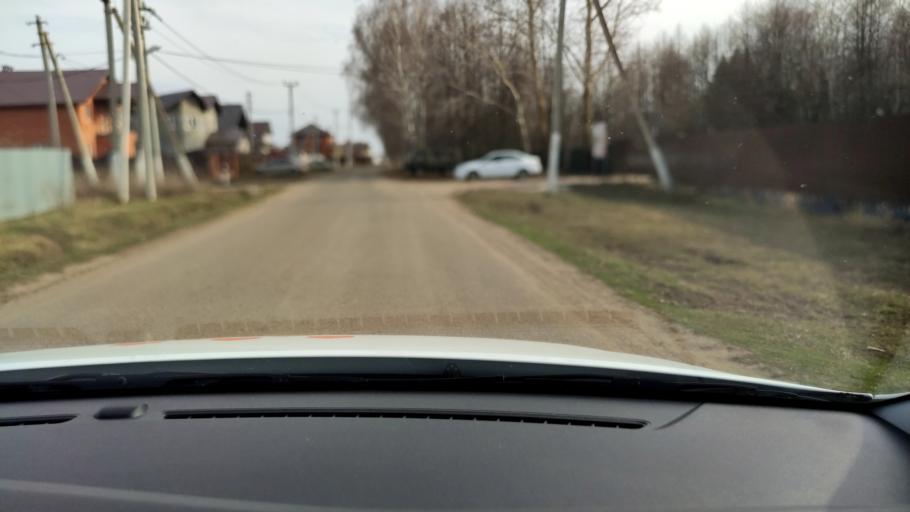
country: RU
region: Tatarstan
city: Stolbishchi
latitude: 55.6449
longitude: 49.3121
